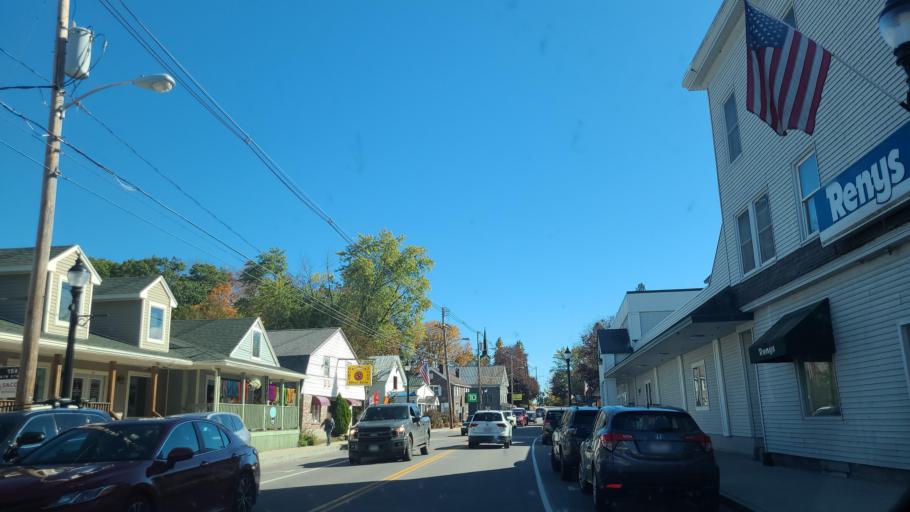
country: US
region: Maine
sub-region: Cumberland County
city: Bridgton
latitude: 44.0545
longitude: -70.7080
